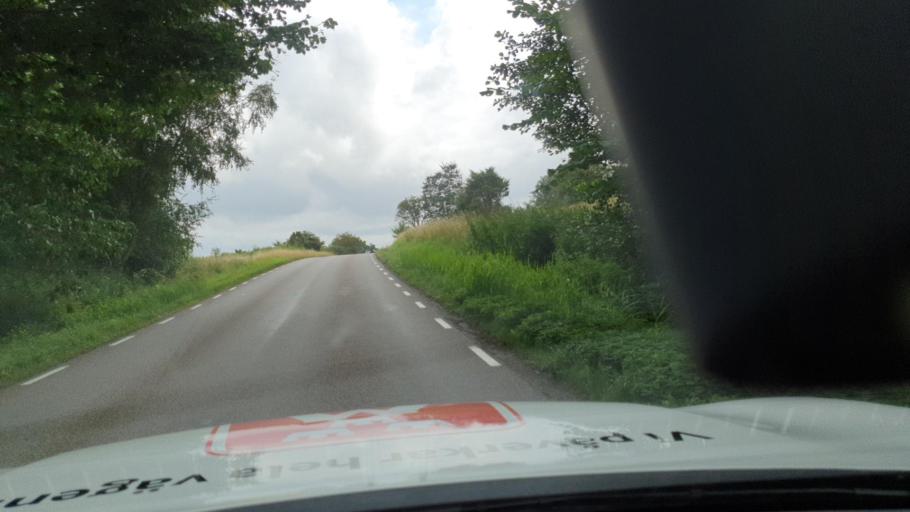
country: SE
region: Vaestra Goetaland
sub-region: Tanums Kommun
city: Grebbestad
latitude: 58.6694
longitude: 11.2958
